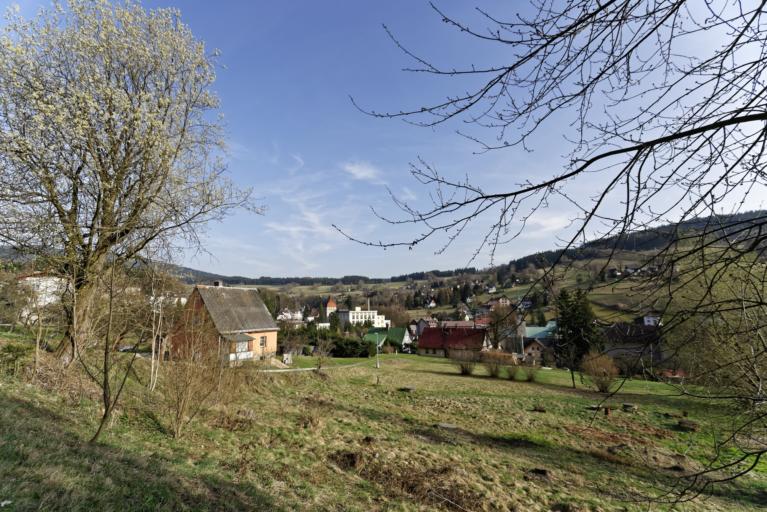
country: CZ
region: Liberecky
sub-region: Okres Semily
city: Rokytnice nad Jizerou
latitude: 50.7308
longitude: 15.4505
